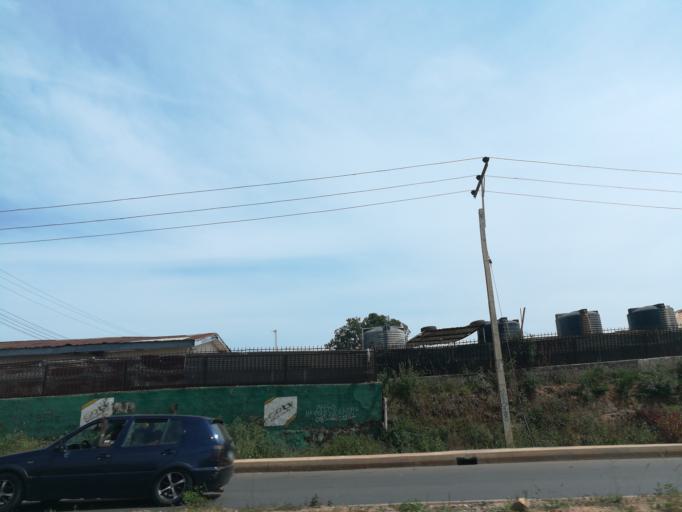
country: NG
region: Plateau
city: Bukuru
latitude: 9.8246
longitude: 8.8654
